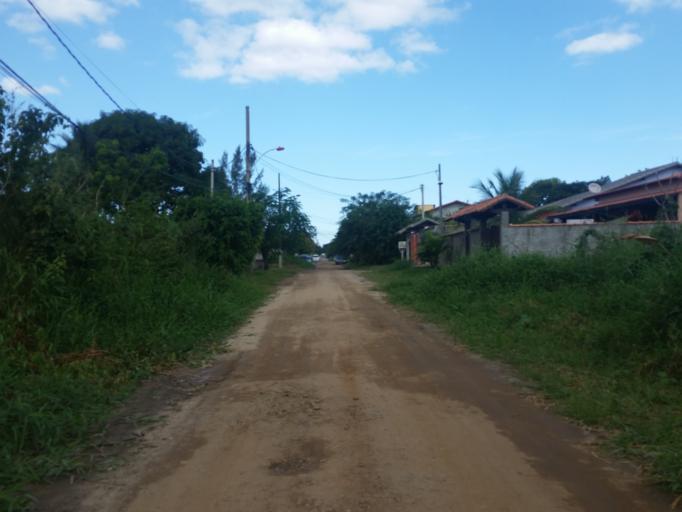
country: BR
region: Rio de Janeiro
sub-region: Marica
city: Marica
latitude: -22.9572
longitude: -42.9667
